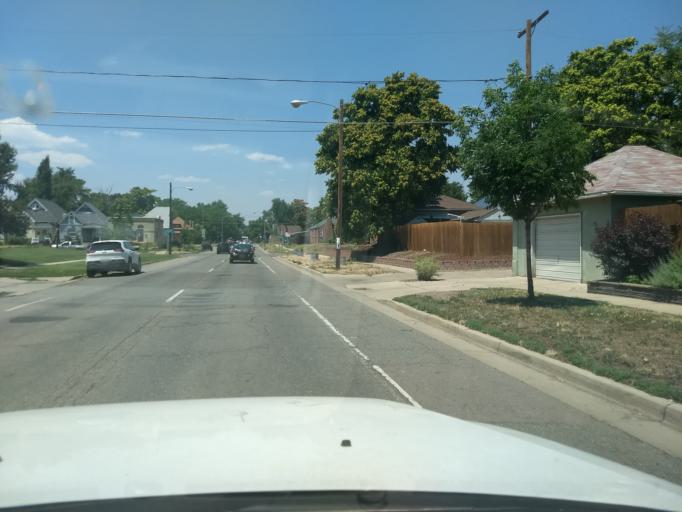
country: US
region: Colorado
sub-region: Denver County
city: Denver
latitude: 39.7620
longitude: -104.9626
